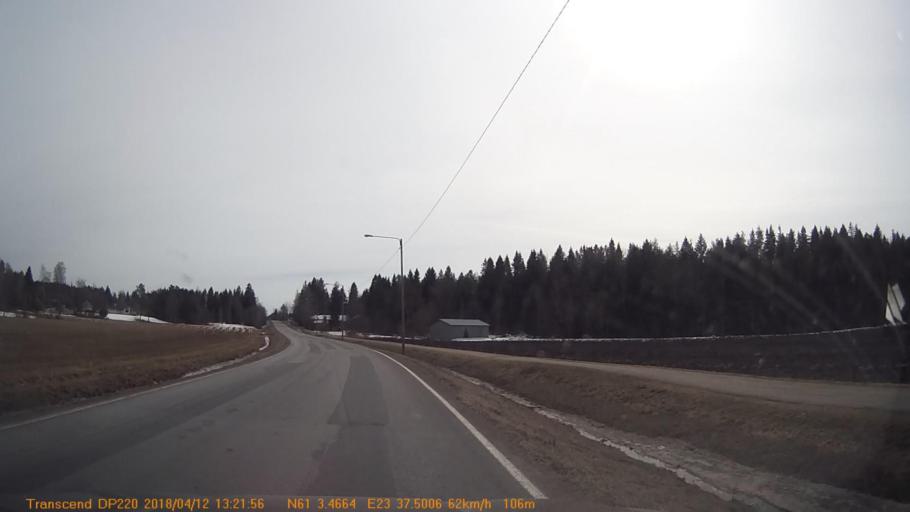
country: FI
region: Pirkanmaa
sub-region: Etelae-Pirkanmaa
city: Urjala
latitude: 61.0565
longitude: 23.6256
